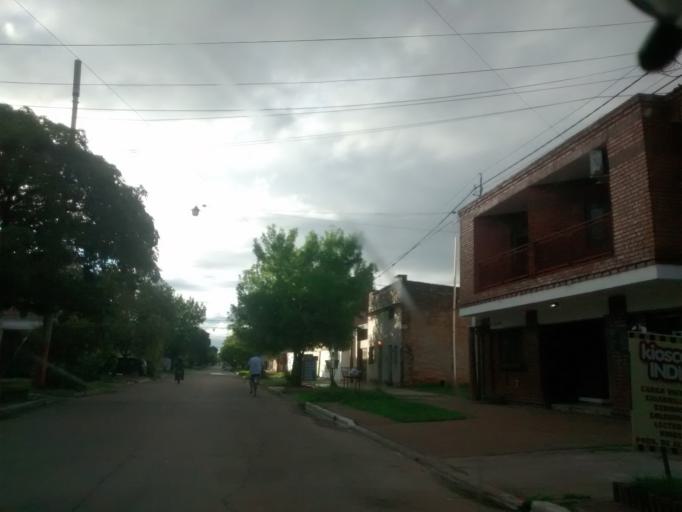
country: AR
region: Chaco
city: Resistencia
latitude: -27.4616
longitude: -58.9765
